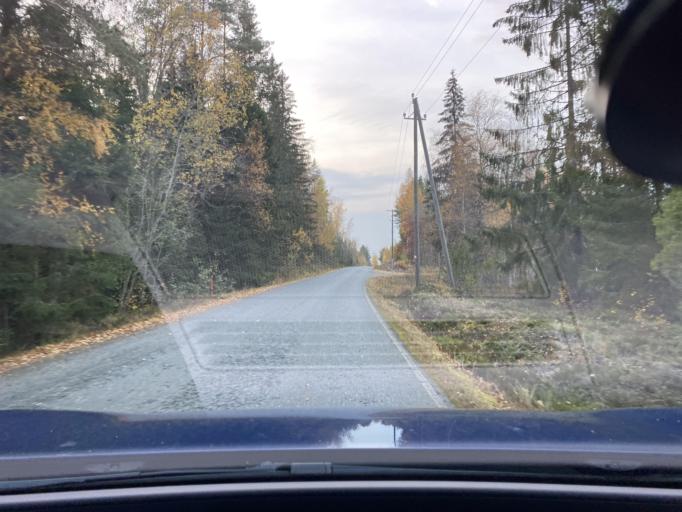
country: FI
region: Varsinais-Suomi
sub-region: Loimaa
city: Alastaro
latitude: 61.0844
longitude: 22.9248
